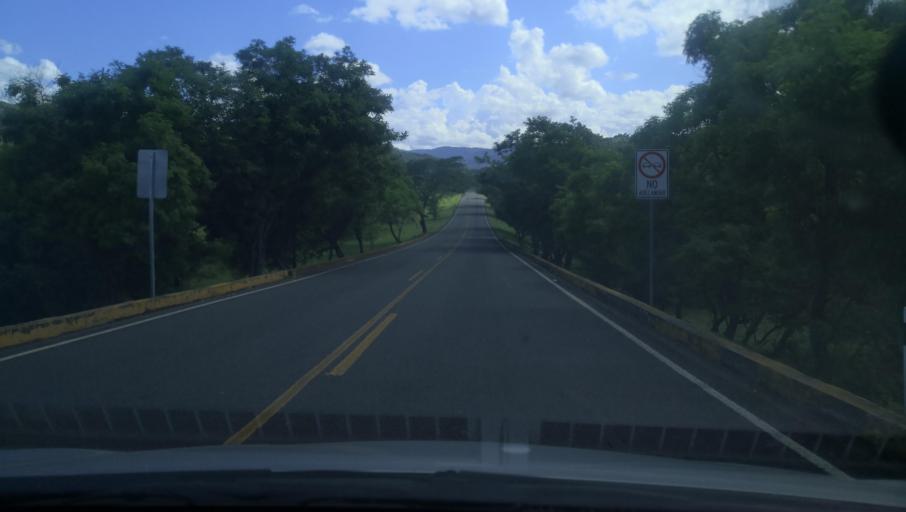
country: NI
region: Madriz
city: Somoto
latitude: 13.4607
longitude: -86.6637
